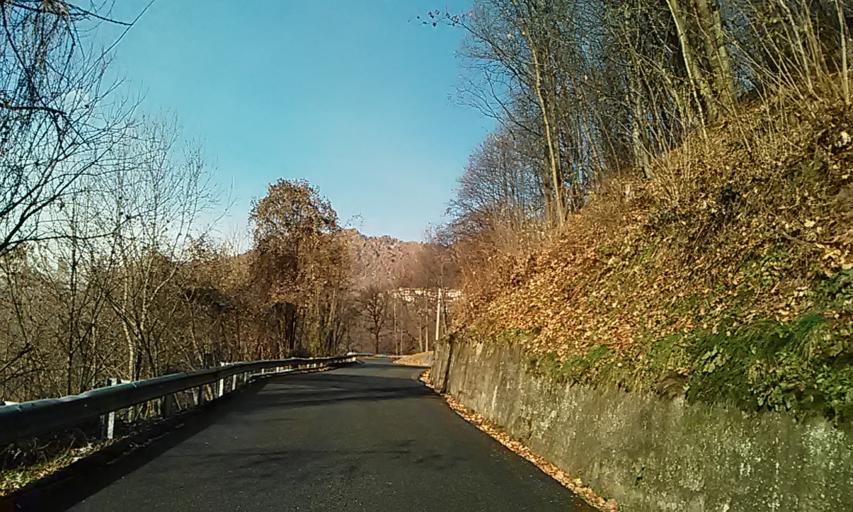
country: IT
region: Piedmont
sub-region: Provincia di Biella
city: Coggiola
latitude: 45.6940
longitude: 8.1784
